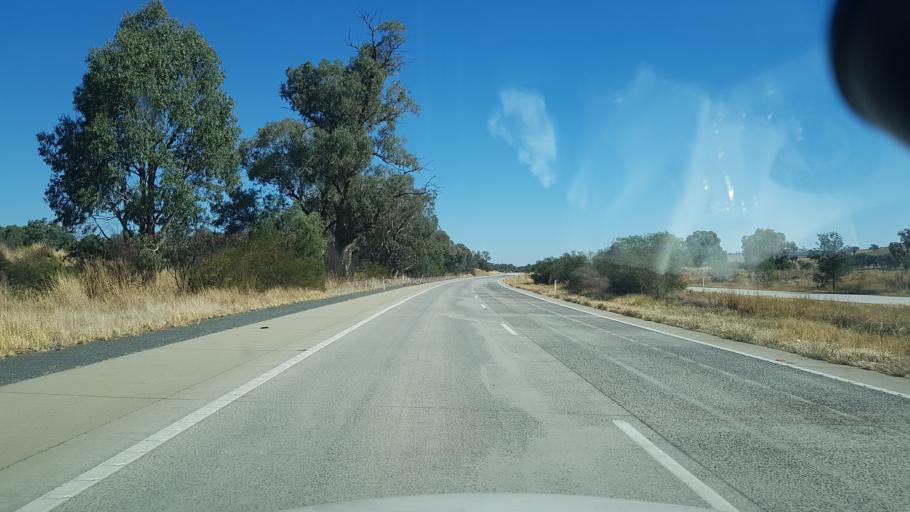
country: AU
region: New South Wales
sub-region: Greater Hume Shire
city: Holbrook
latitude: -35.9043
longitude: 147.1629
